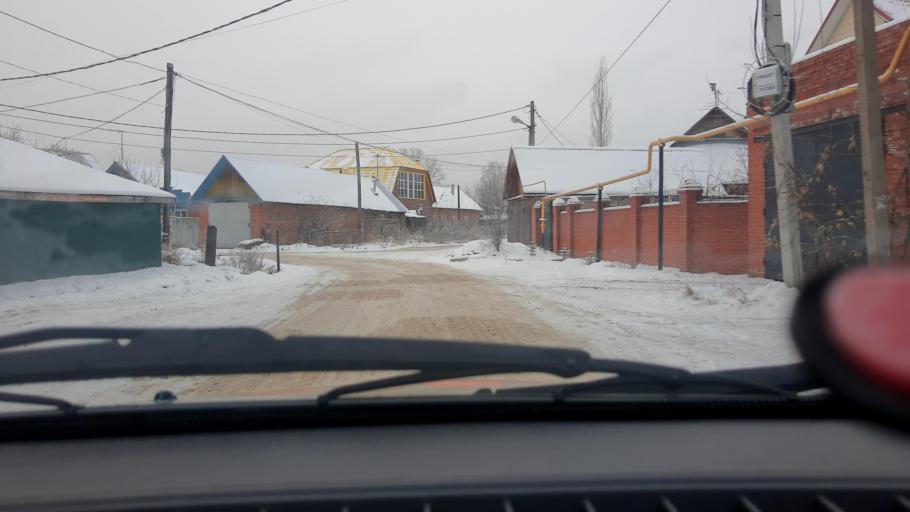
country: RU
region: Bashkortostan
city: Ufa
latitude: 54.8300
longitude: 56.1793
